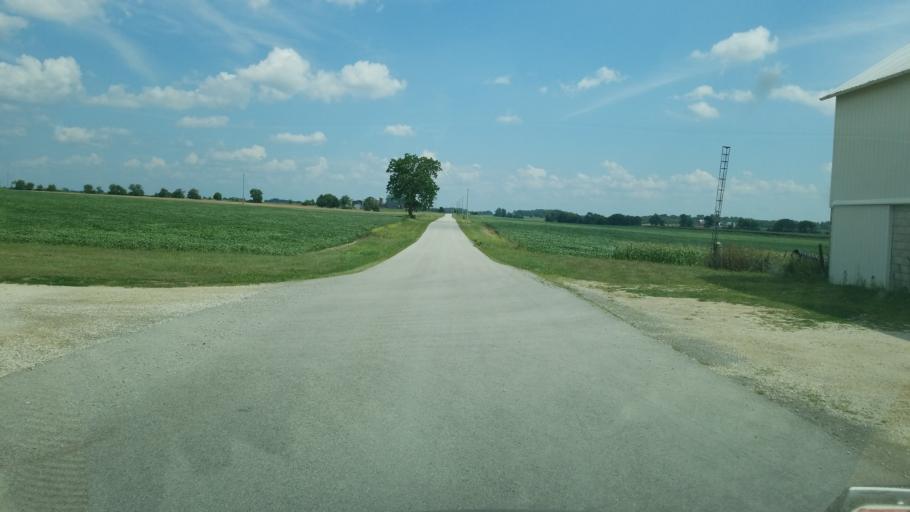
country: US
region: Ohio
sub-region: Wyandot County
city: Carey
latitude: 40.9531
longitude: -83.4798
